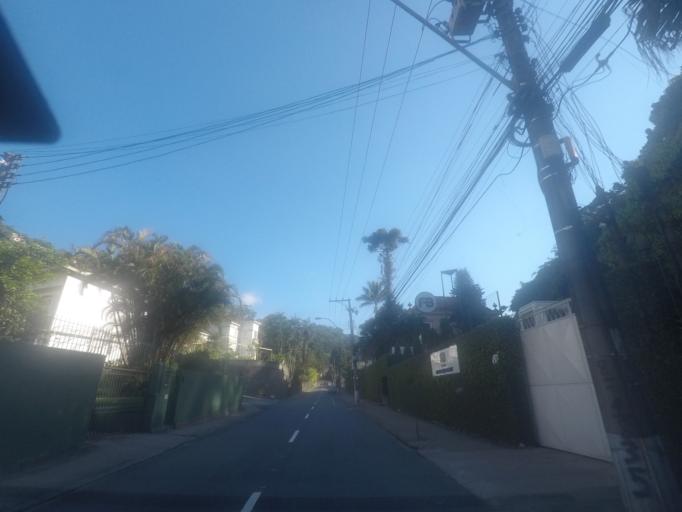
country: BR
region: Rio de Janeiro
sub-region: Petropolis
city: Petropolis
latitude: -22.5109
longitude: -43.1670
